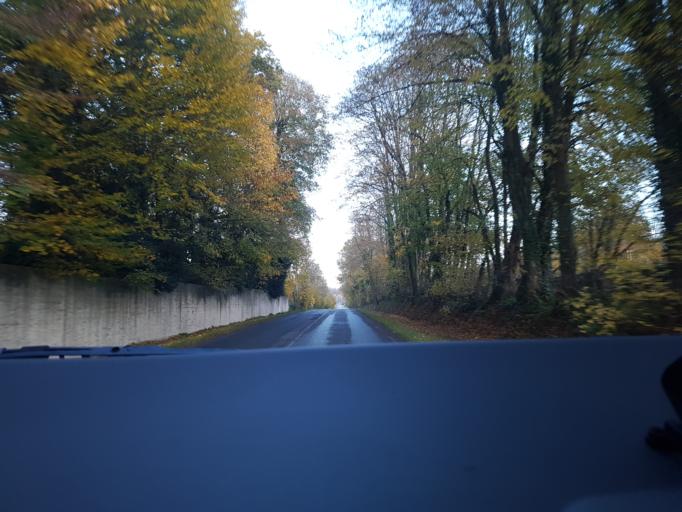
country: FR
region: Lower Normandy
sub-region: Departement du Calvados
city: Dozule
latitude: 49.2492
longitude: 0.0088
